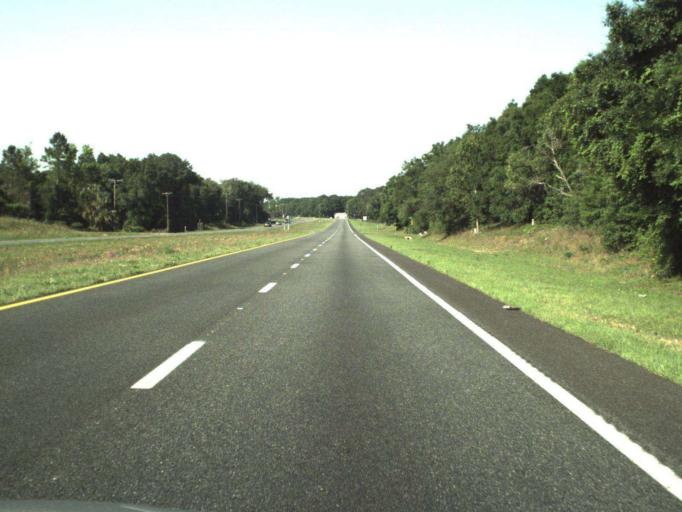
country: US
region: Florida
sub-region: Marion County
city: Citra
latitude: 29.3946
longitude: -82.1194
